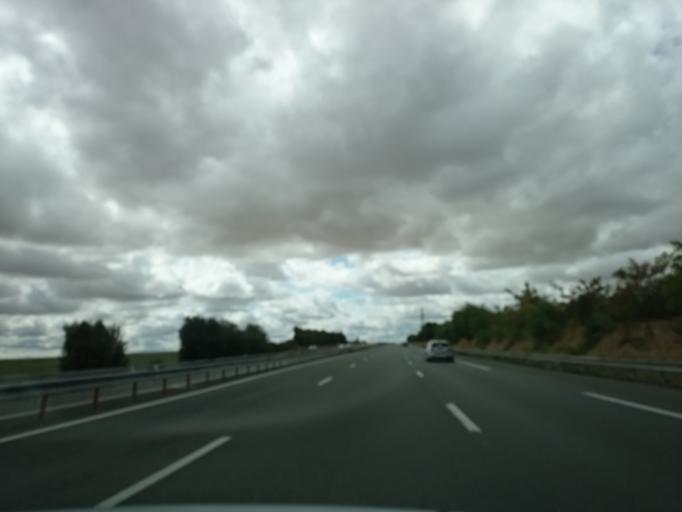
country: FR
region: Centre
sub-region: Departement d'Eure-et-Loir
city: Morancez
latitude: 48.3943
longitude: 1.4953
